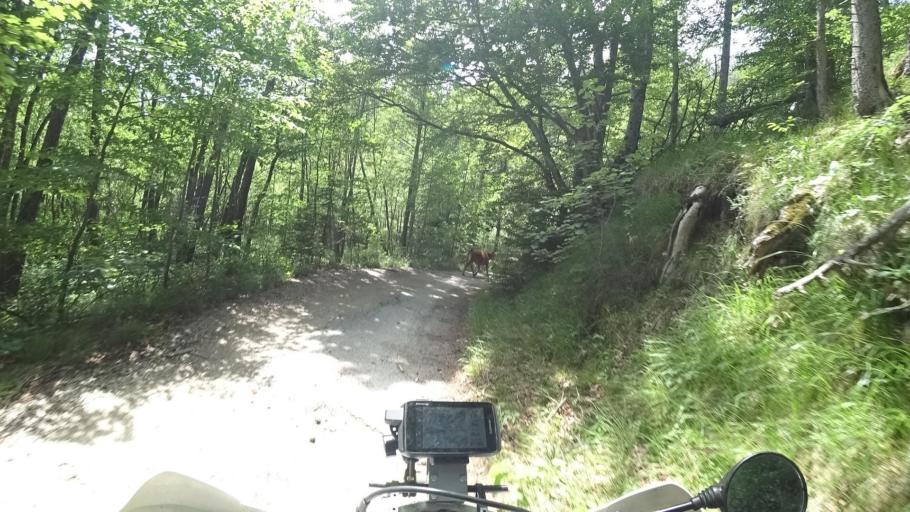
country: HR
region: Licko-Senjska
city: Jezerce
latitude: 44.8455
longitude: 15.6001
